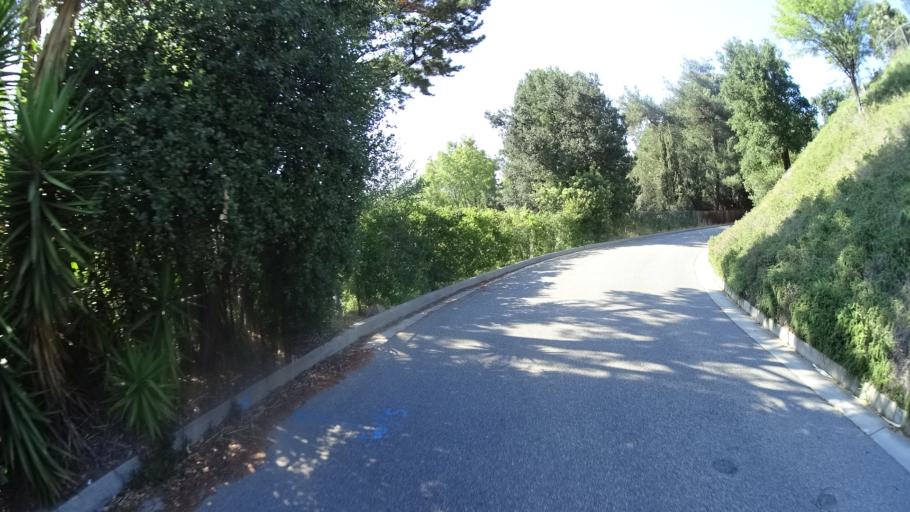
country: US
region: California
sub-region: Los Angeles County
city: Universal City
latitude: 34.1342
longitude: -118.3769
